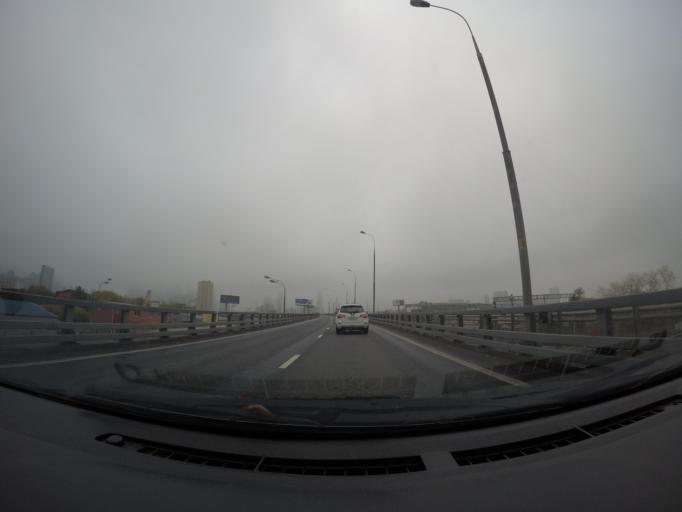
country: RU
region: Moskovskaya
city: Presnenskiy
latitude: 55.7682
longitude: 37.5394
